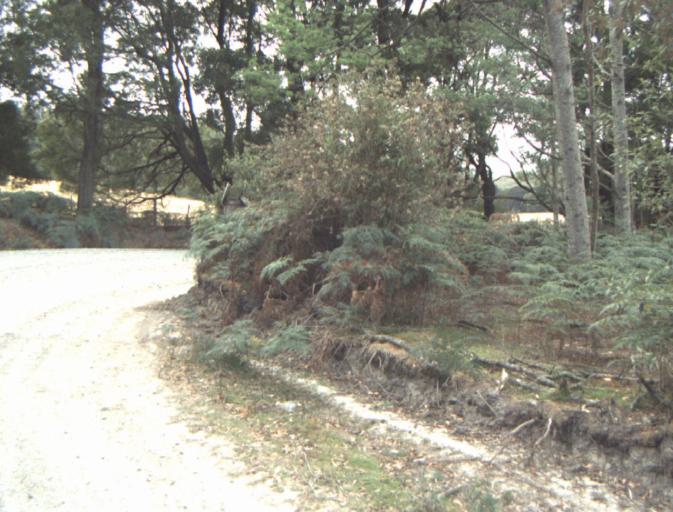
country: AU
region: Tasmania
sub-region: Launceston
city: Mayfield
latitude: -41.1922
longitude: 147.1604
